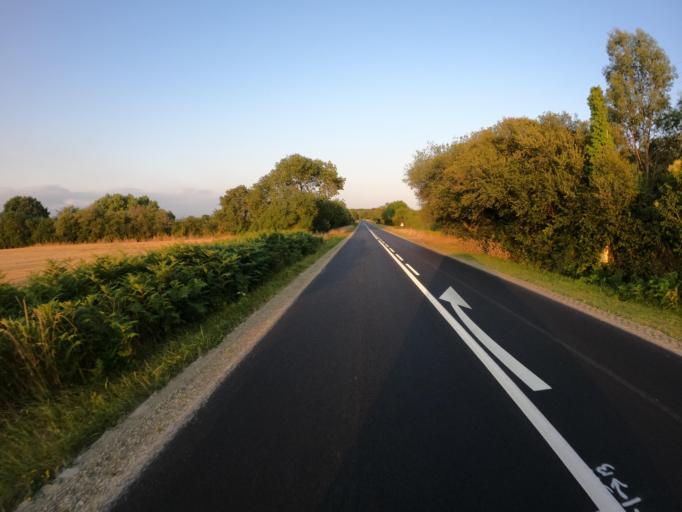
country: FR
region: Pays de la Loire
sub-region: Departement de la Sarthe
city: Auvers-le-Hamon
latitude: 47.8668
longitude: -0.4201
